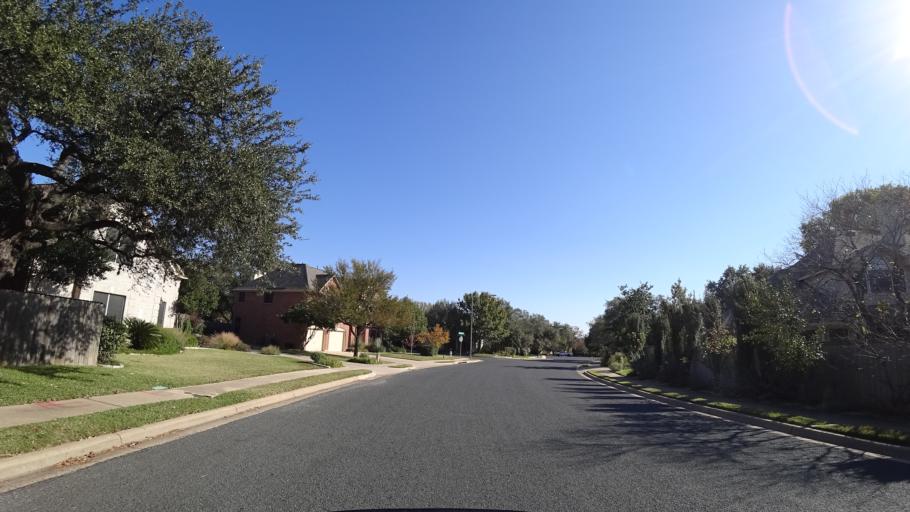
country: US
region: Texas
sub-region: Travis County
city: Shady Hollow
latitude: 30.2246
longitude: -97.8723
